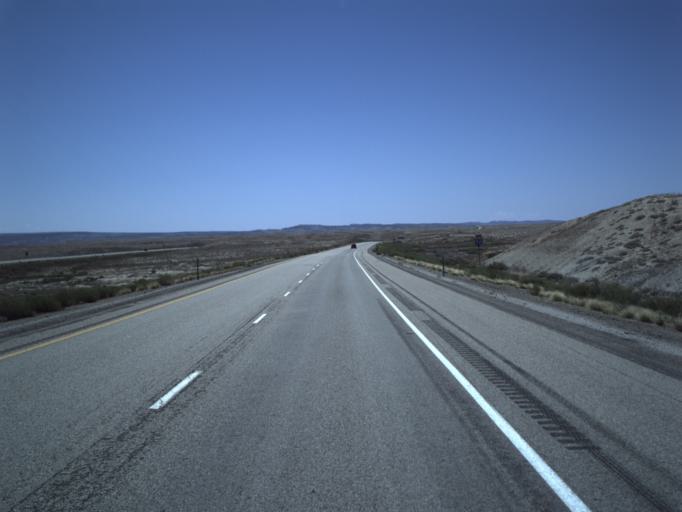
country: US
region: Utah
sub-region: Grand County
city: Moab
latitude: 38.9870
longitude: -109.3390
